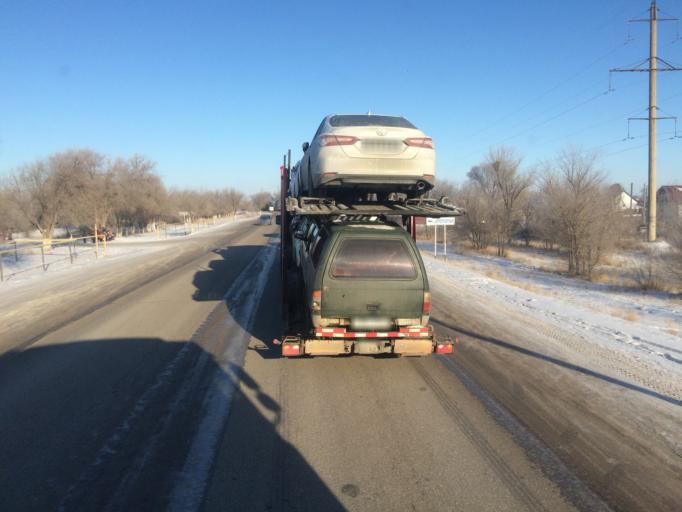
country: KZ
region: Aqtoebe
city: Aqtobe
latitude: 50.2658
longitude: 57.2637
